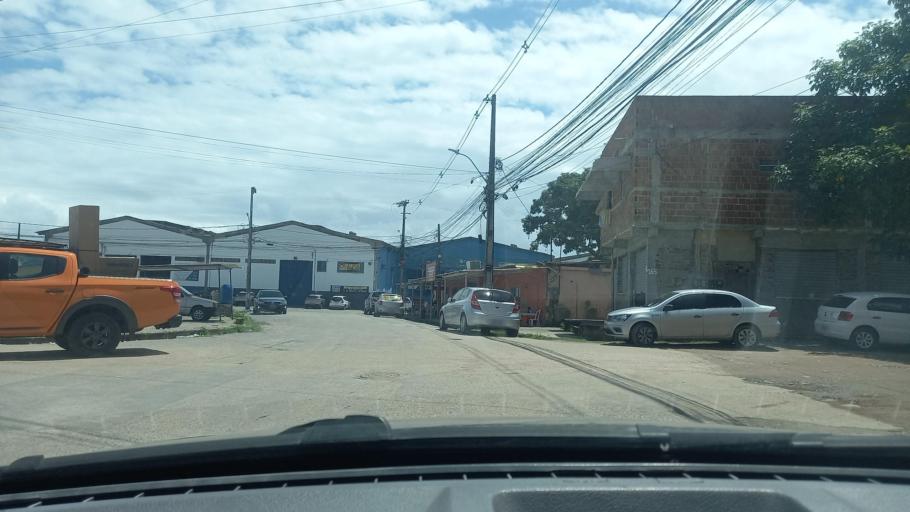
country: BR
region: Pernambuco
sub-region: Recife
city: Recife
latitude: -8.1041
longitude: -34.9093
